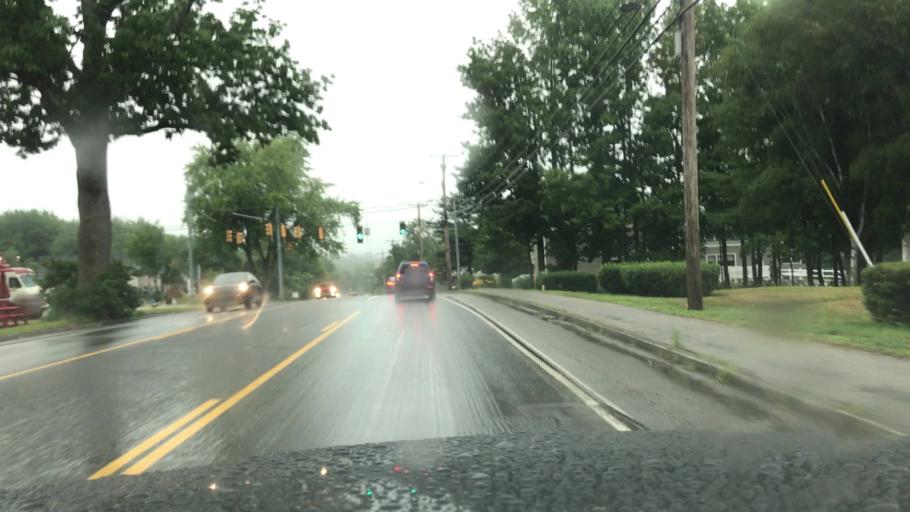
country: US
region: Maine
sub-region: York County
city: Kennebunk
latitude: 43.3989
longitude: -70.5288
